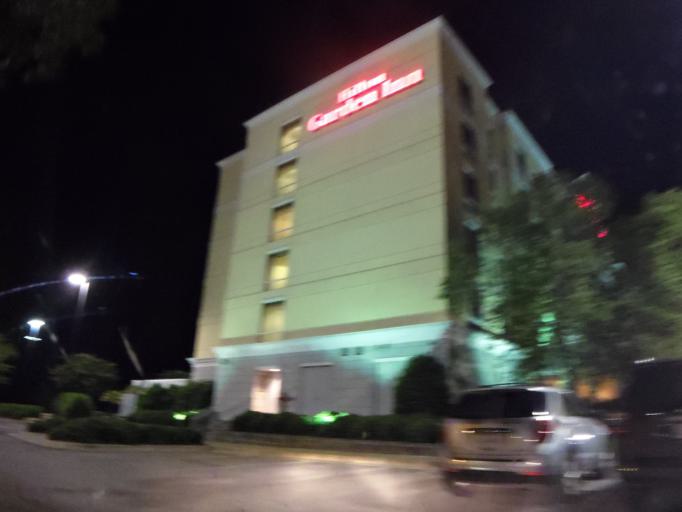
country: US
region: Mississippi
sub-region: Lauderdale County
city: Meridian
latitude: 32.3691
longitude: -88.6742
